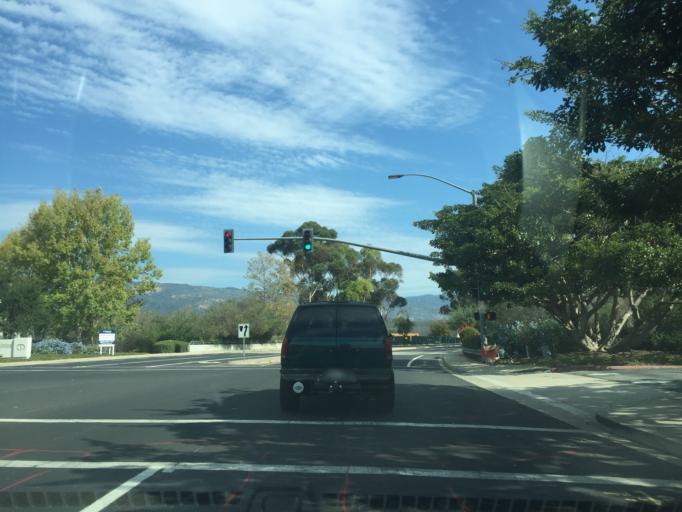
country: US
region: California
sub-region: Santa Barbara County
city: Isla Vista
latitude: 34.4315
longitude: -119.8594
